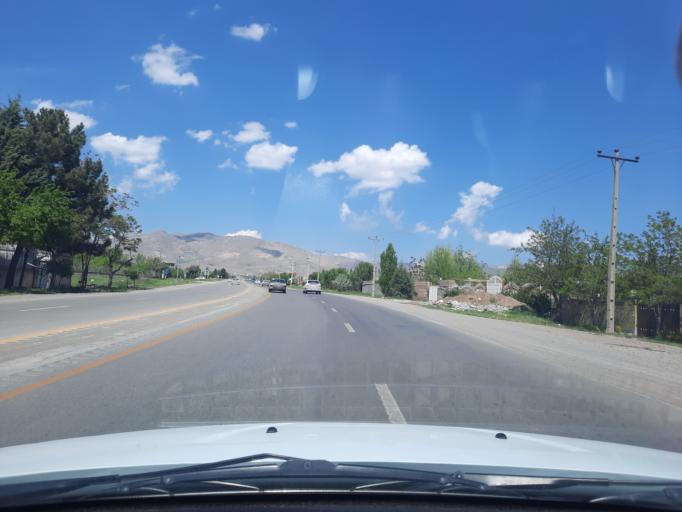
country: IR
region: Qazvin
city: Alvand
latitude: 36.3013
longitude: 50.1434
